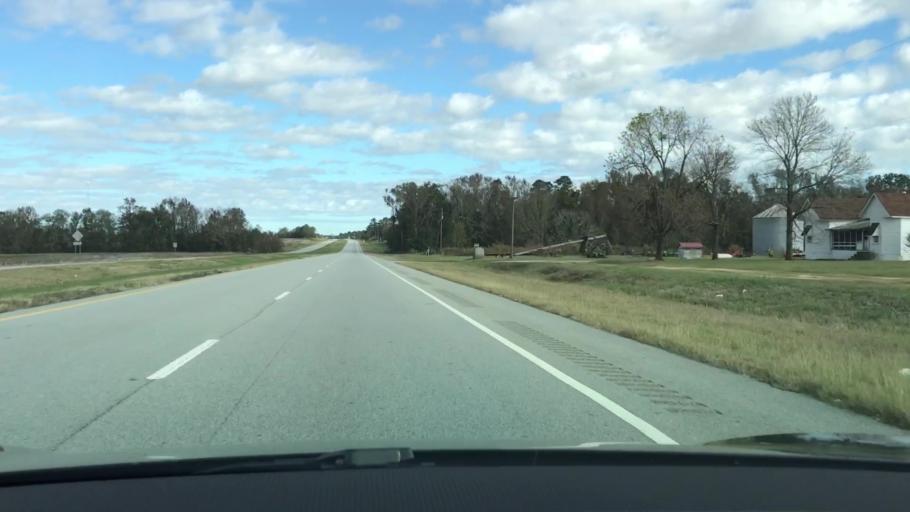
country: US
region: Georgia
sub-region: Jefferson County
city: Wadley
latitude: 32.8323
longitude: -82.4012
